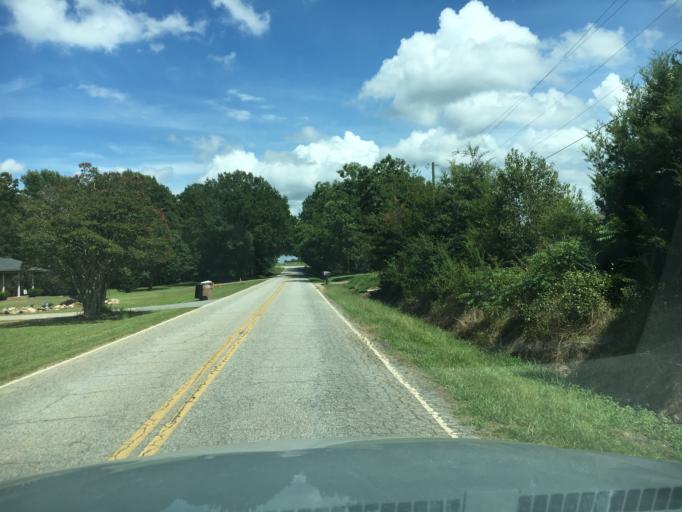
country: US
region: South Carolina
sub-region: Anderson County
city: Belton
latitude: 34.5649
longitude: -82.4739
